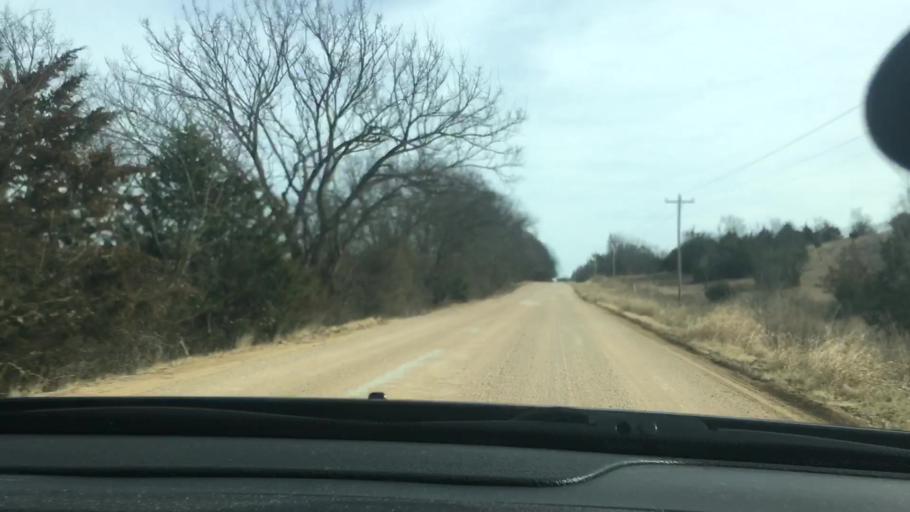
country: US
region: Oklahoma
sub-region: Murray County
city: Sulphur
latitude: 34.4060
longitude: -96.9403
